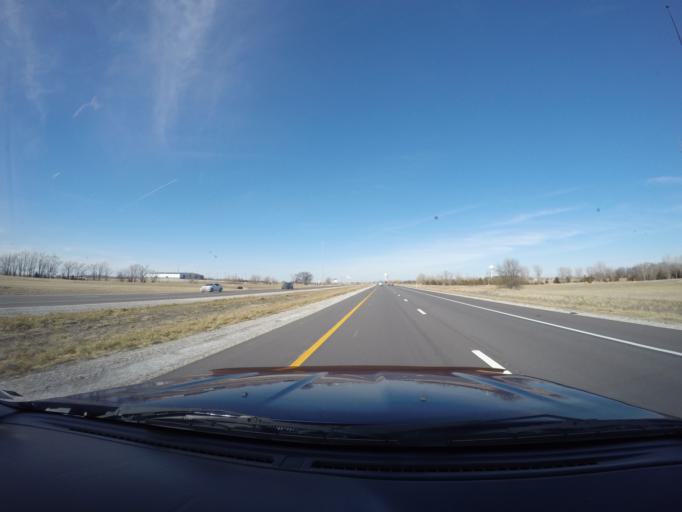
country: US
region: Kansas
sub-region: Sedgwick County
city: Park City
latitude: 37.8265
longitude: -97.3265
